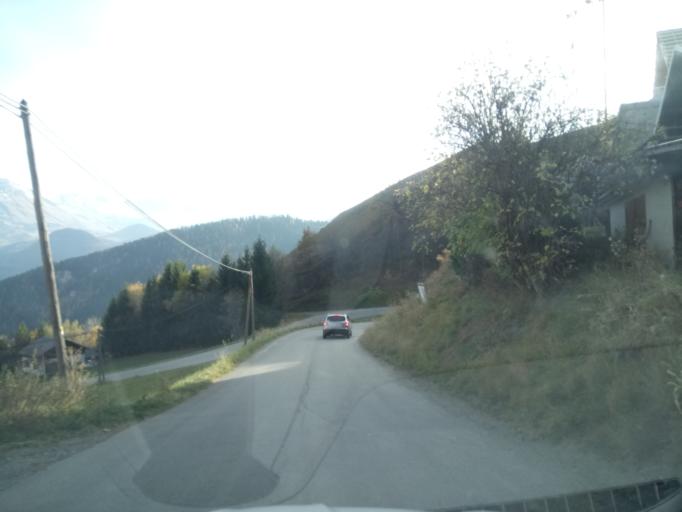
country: FR
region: Rhone-Alpes
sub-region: Departement de la Savoie
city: Saint-Jean-de-Maurienne
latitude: 45.2784
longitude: 6.3089
